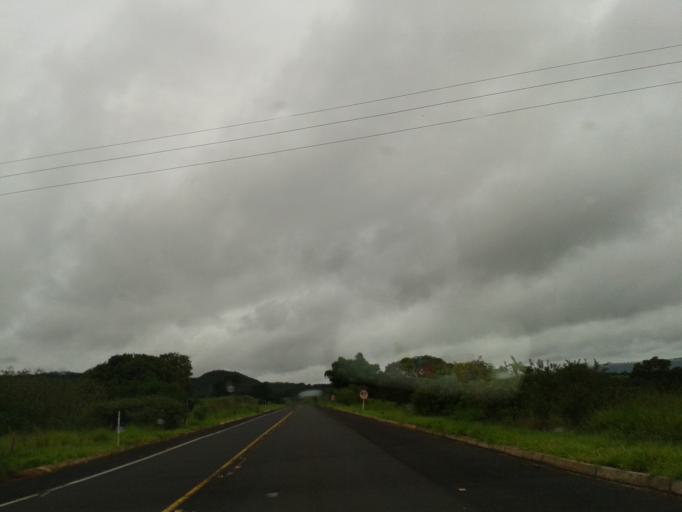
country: BR
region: Minas Gerais
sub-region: Santa Vitoria
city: Santa Vitoria
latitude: -19.2055
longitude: -50.0250
